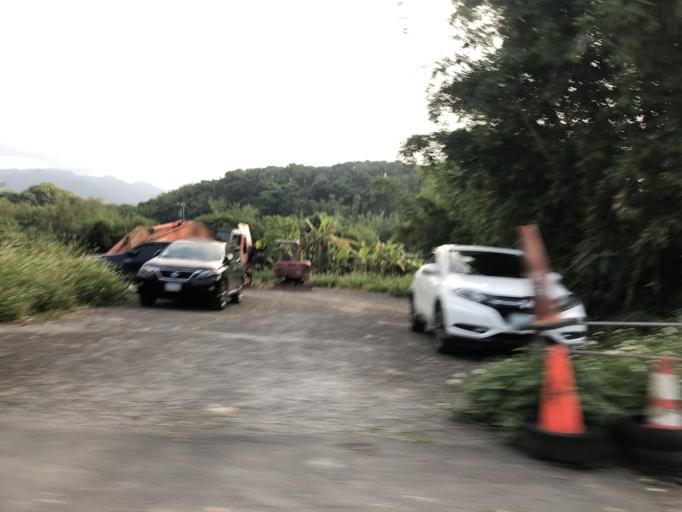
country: TW
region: Taiwan
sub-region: Keelung
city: Keelung
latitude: 25.2168
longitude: 121.6422
